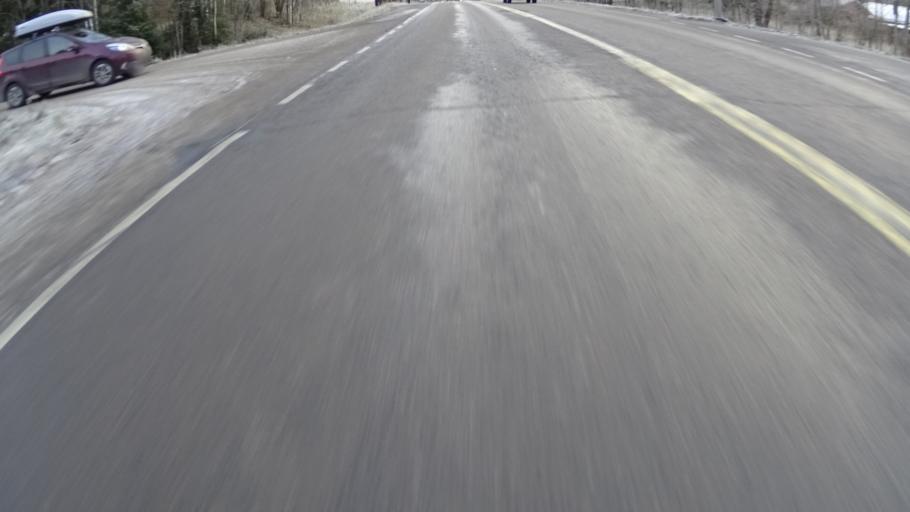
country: FI
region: Uusimaa
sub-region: Helsinki
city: Nurmijaervi
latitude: 60.3980
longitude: 24.7340
